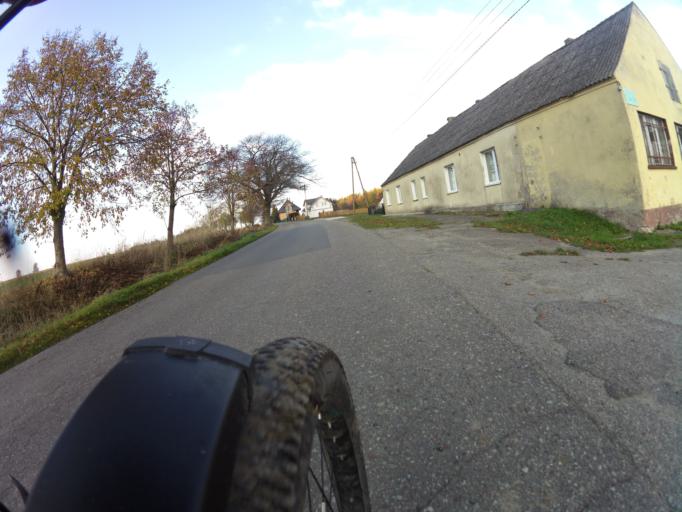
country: PL
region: Pomeranian Voivodeship
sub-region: Powiat pucki
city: Krokowa
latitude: 54.7538
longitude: 18.1844
